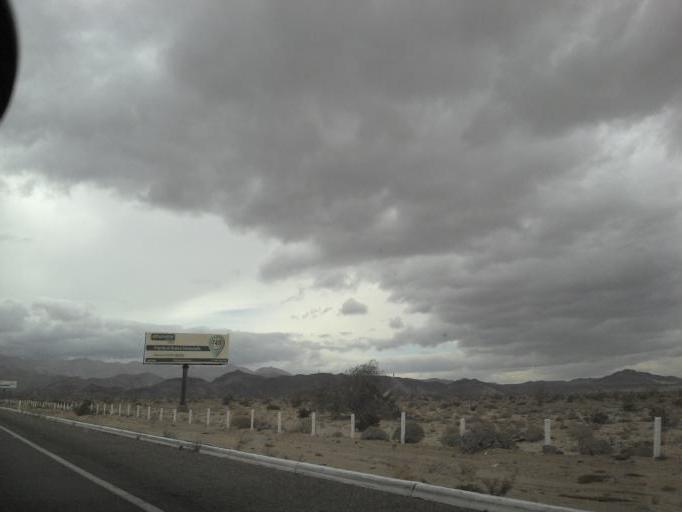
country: US
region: California
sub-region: Imperial County
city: Seeley
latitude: 32.5660
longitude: -115.9093
